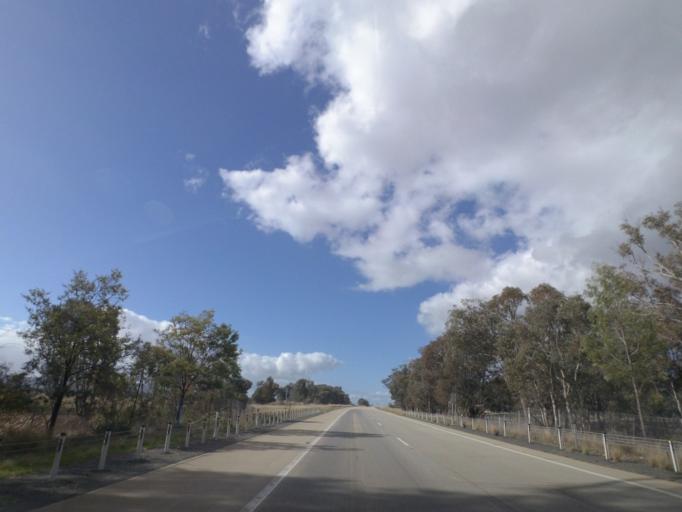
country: AU
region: New South Wales
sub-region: Greater Hume Shire
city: Holbrook
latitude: -35.6872
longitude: 147.3532
